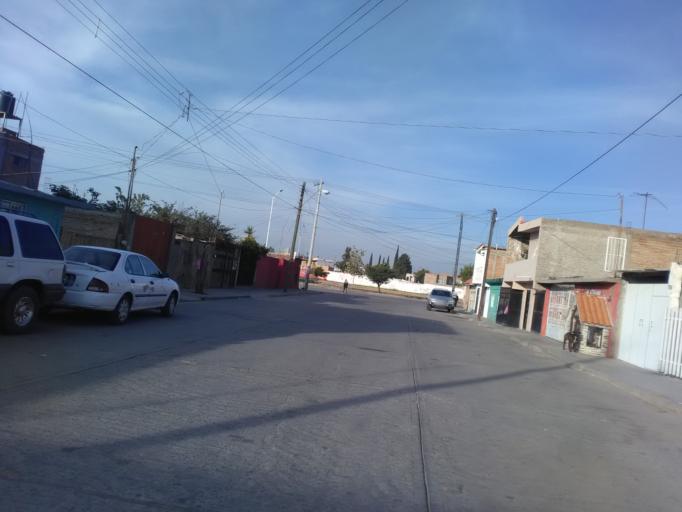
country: MX
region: Durango
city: Victoria de Durango
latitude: 24.0430
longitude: -104.6500
